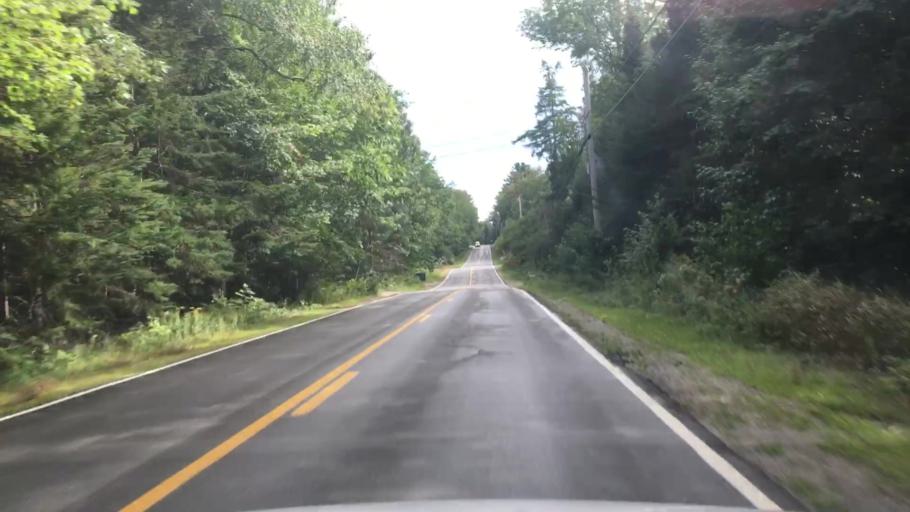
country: US
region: Maine
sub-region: Hancock County
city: Trenton
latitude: 44.4553
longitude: -68.4254
